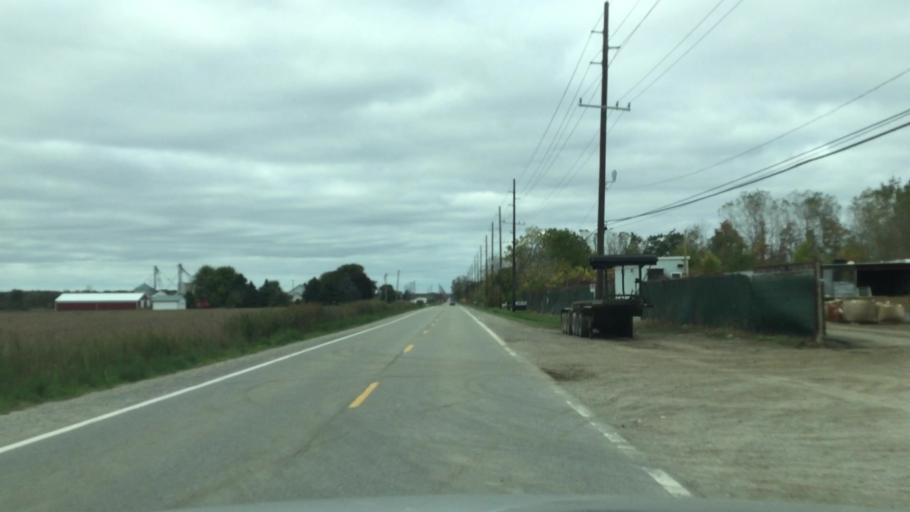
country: US
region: Michigan
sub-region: Macomb County
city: Richmond
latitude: 42.8083
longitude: -82.7964
